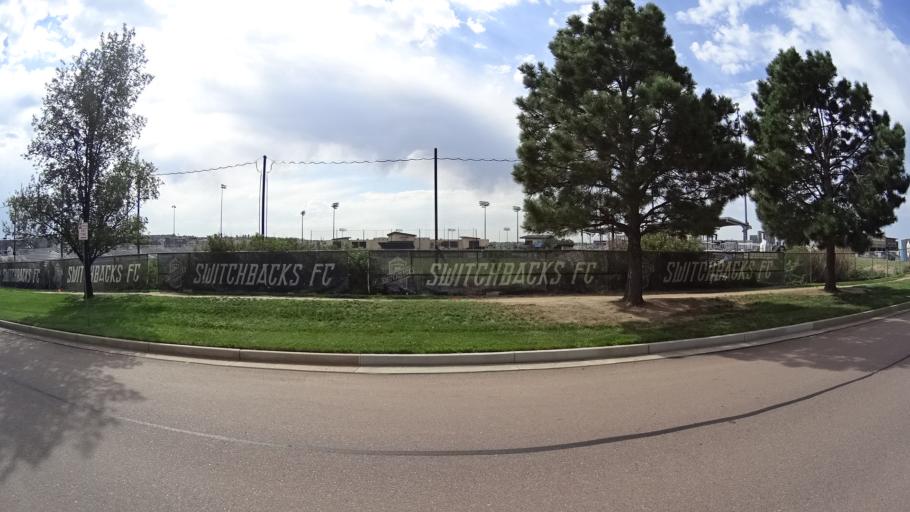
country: US
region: Colorado
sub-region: El Paso County
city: Cimarron Hills
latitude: 38.8960
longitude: -104.7122
